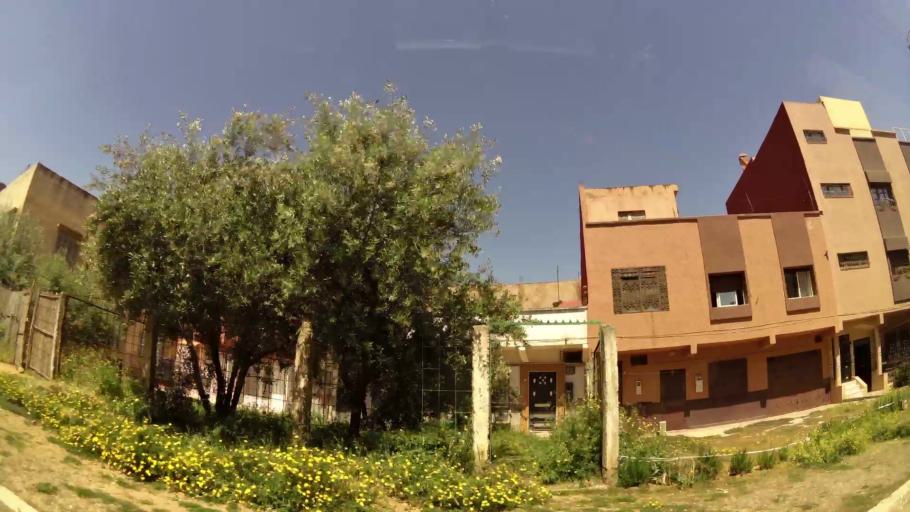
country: MA
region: Rabat-Sale-Zemmour-Zaer
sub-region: Khemisset
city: Khemisset
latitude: 33.8126
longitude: -6.0721
